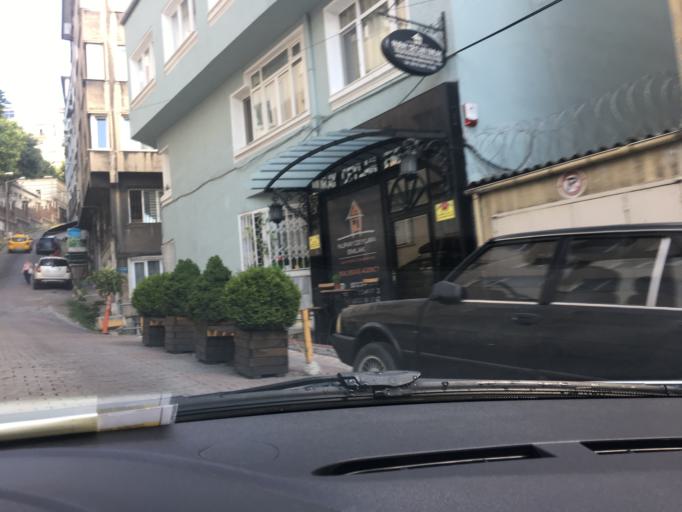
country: TR
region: Istanbul
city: Eminoenue
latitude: 41.0354
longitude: 28.9907
